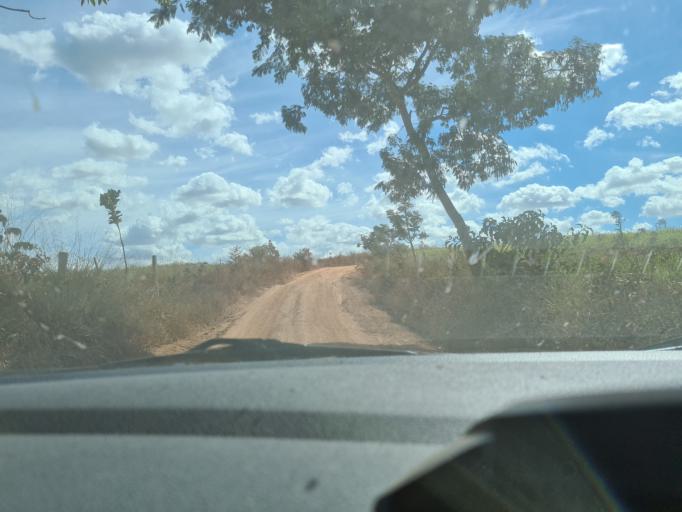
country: BR
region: Goias
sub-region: Silvania
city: Silvania
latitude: -16.5341
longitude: -48.5864
